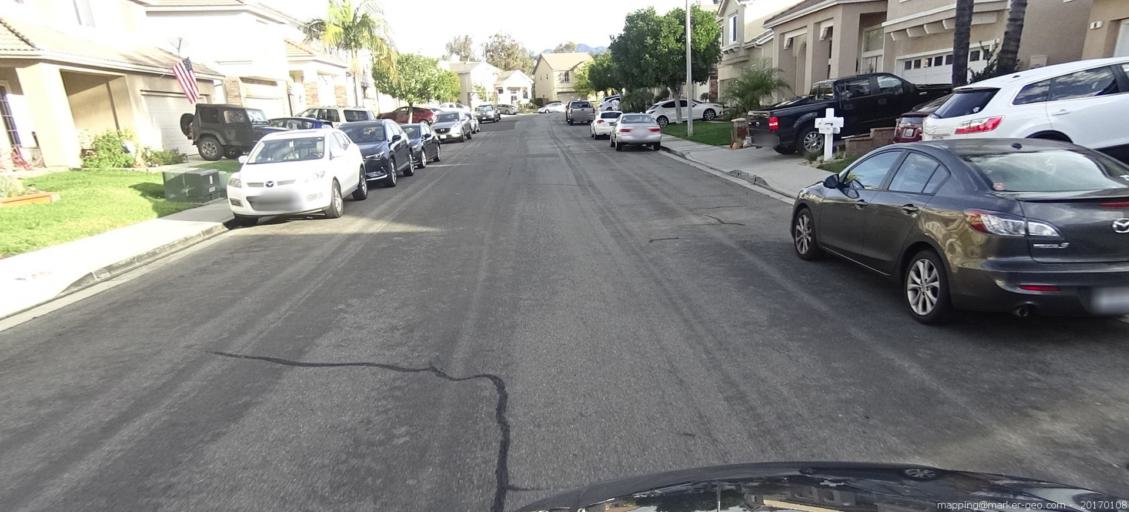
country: US
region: California
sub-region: Orange County
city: Las Flores
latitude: 33.5935
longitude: -117.6245
